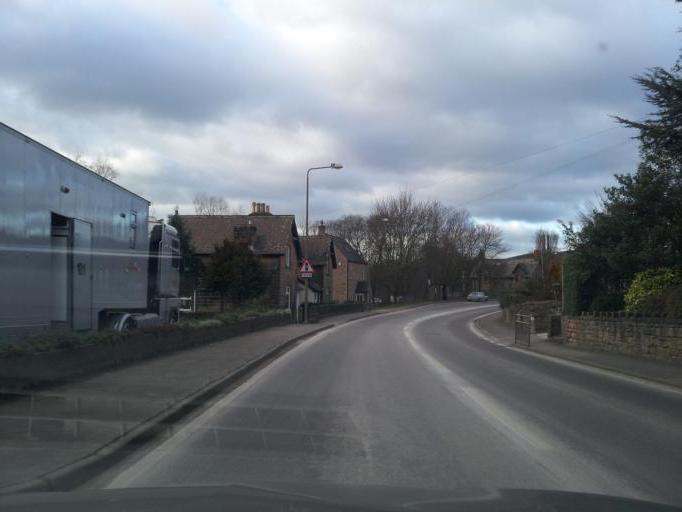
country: GB
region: England
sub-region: Derbyshire
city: Matlock
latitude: 53.1762
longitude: -1.6088
